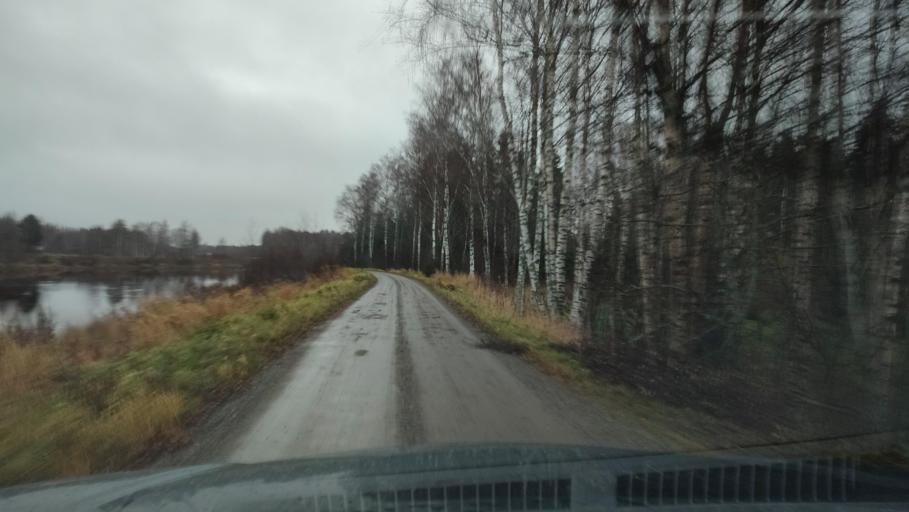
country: FI
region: Ostrobothnia
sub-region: Sydosterbotten
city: Kristinestad
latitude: 62.2374
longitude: 21.4653
